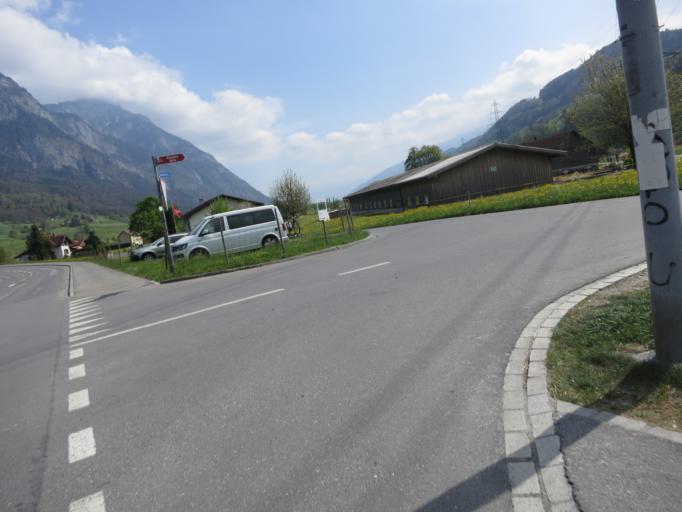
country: CH
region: Saint Gallen
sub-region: Wahlkreis Sarganserland
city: Flums
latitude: 47.0890
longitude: 9.3543
